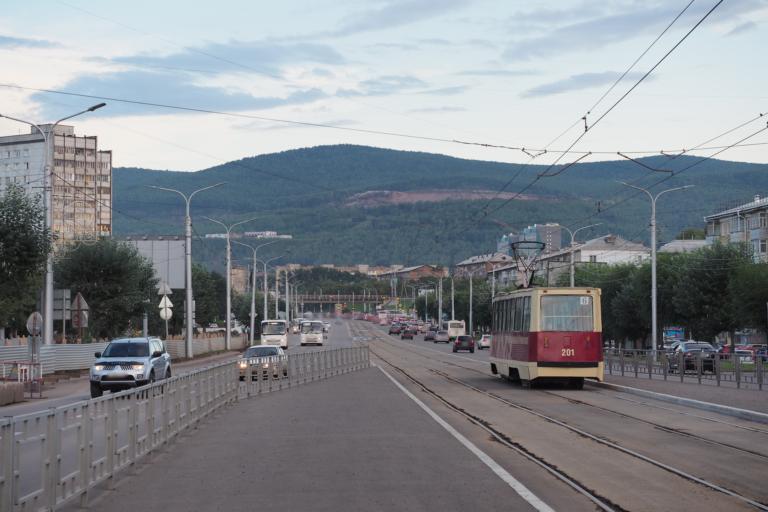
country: RU
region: Krasnoyarskiy
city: Krasnoyarsk
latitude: 55.9903
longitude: 92.8868
